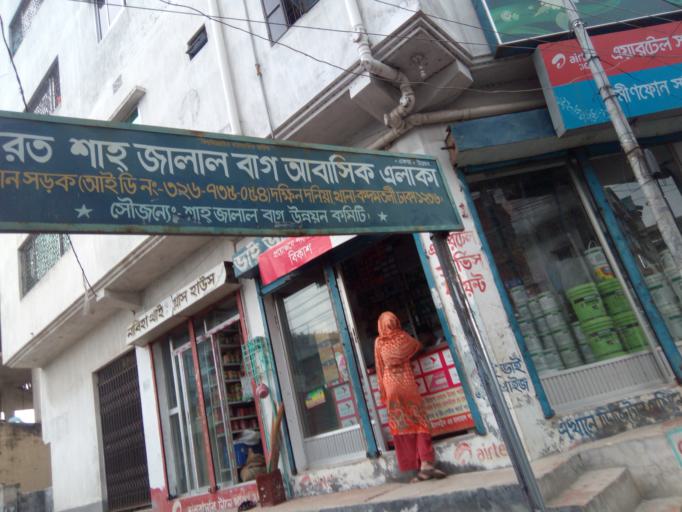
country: BD
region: Dhaka
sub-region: Dhaka
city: Dhaka
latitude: 23.6907
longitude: 90.4474
